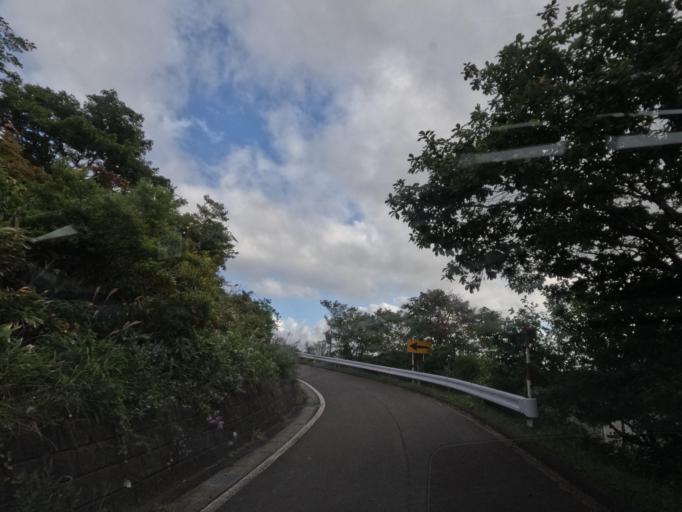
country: JP
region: Hokkaido
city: Muroran
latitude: 42.3200
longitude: 141.0026
